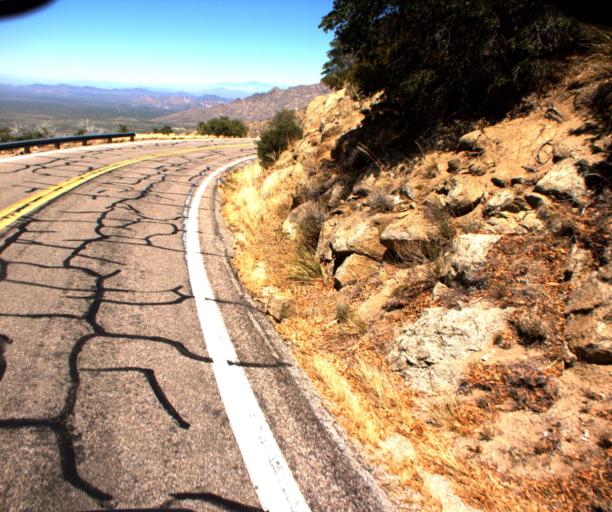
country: US
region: Arizona
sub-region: Pima County
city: Sells
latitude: 31.9720
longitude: -111.6203
